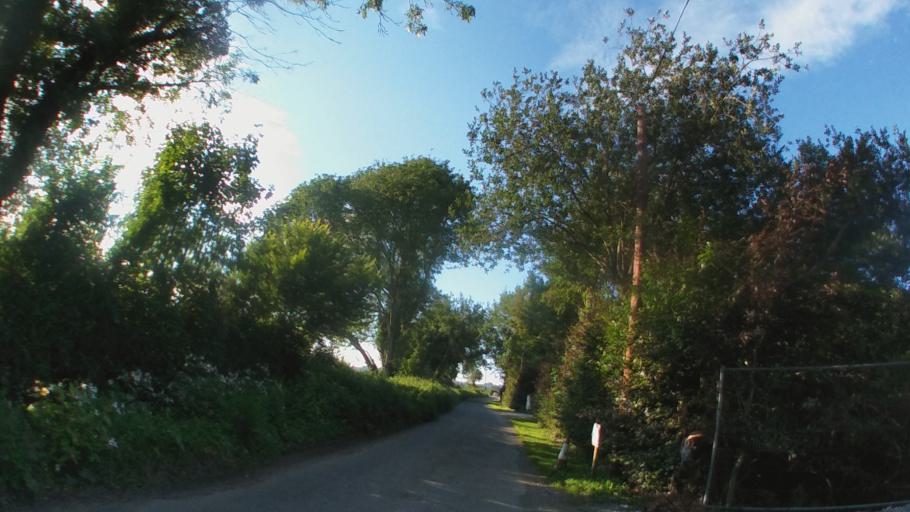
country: IE
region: Leinster
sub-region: Kilkenny
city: Kilkenny
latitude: 52.6914
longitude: -7.1889
